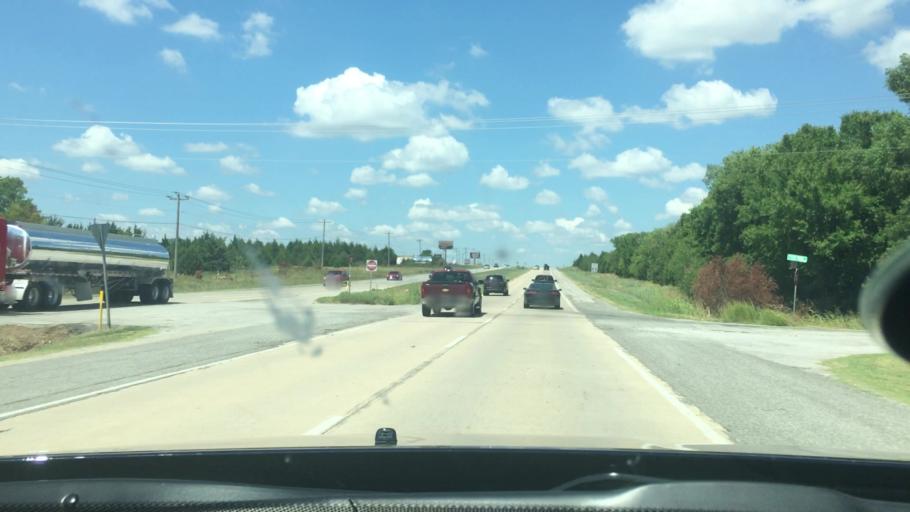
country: US
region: Oklahoma
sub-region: Carter County
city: Lone Grove
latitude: 34.1730
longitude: -97.2125
